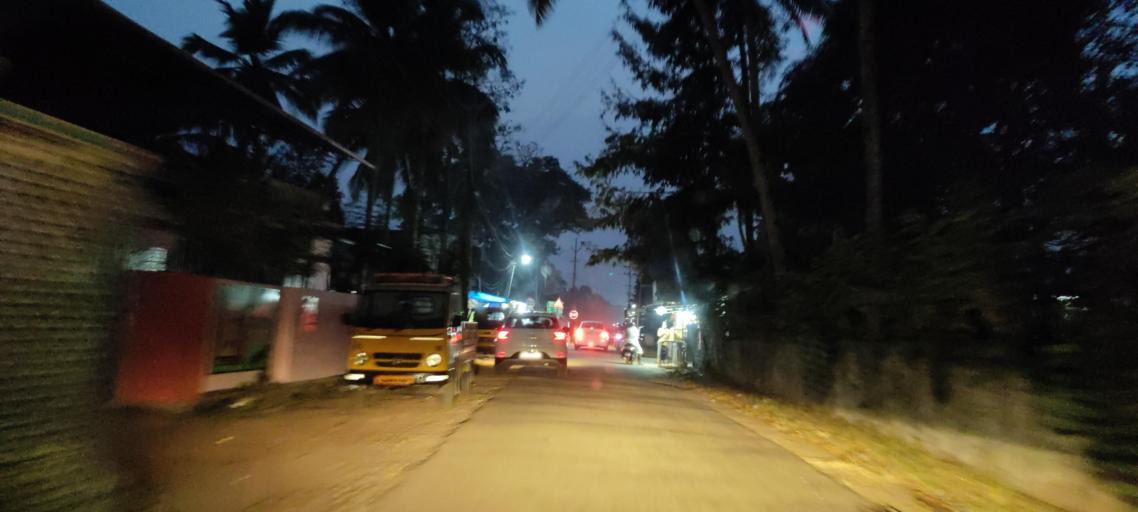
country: IN
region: Kerala
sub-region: Alappuzha
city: Mavelikara
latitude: 9.3195
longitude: 76.4255
